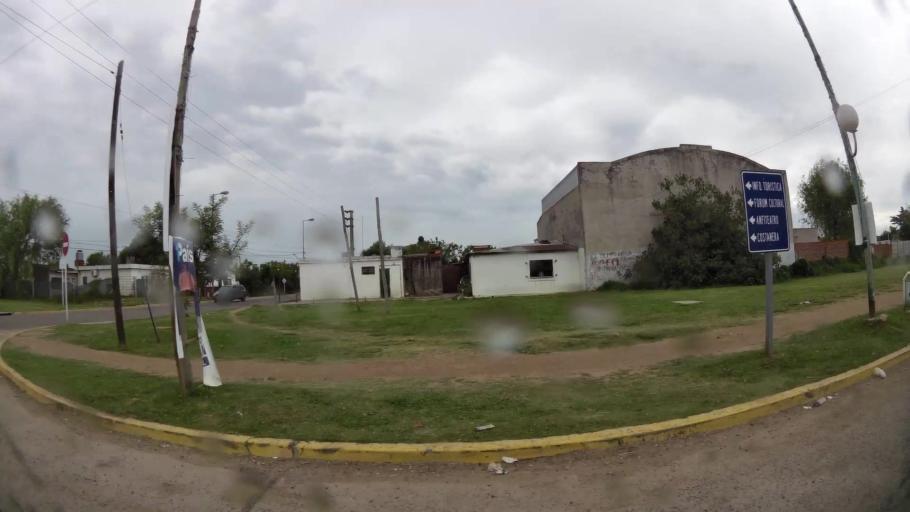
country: AR
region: Buenos Aires
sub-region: Partido de Zarate
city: Zarate
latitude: -34.1078
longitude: -59.0291
